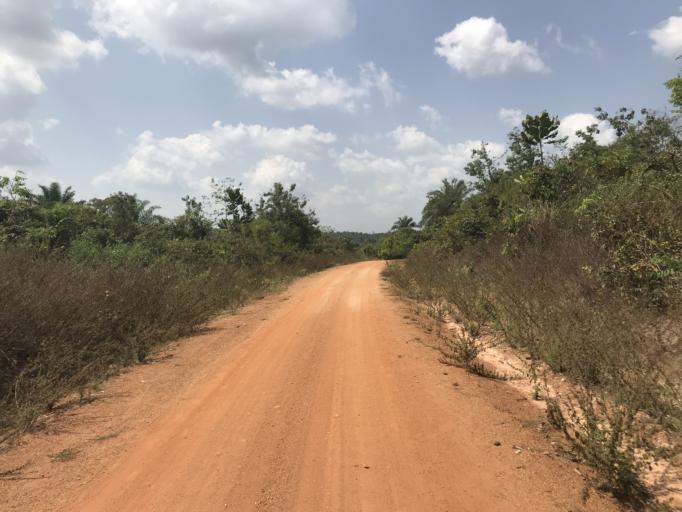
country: NG
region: Osun
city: Ifon
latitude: 7.9789
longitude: 4.5168
